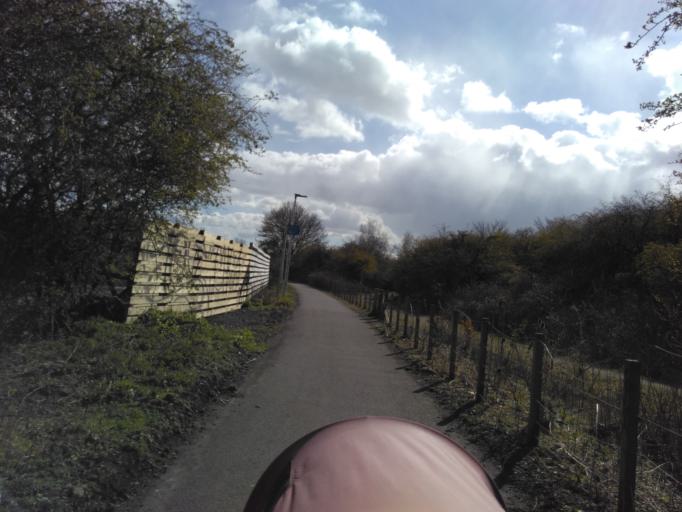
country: GB
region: Scotland
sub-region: Midlothian
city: Loanhead
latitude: 55.8890
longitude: -3.1469
